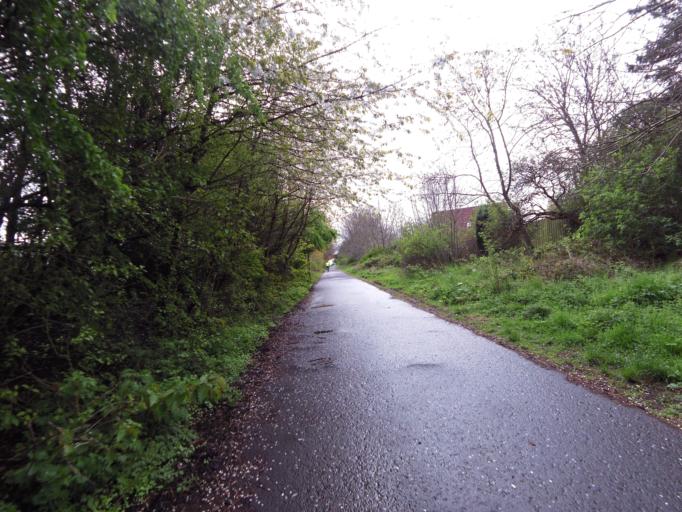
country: GB
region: Scotland
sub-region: Edinburgh
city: Colinton
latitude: 55.9654
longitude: -3.2636
